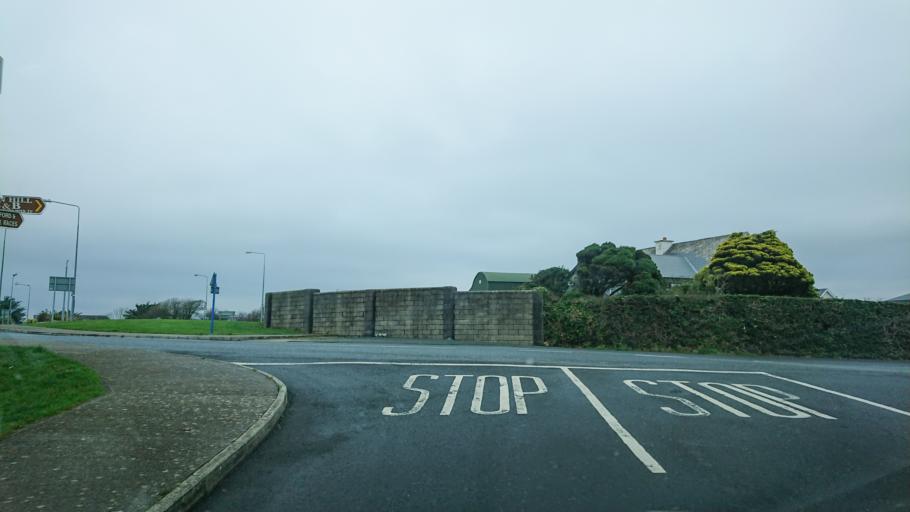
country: IE
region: Munster
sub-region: Waterford
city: Tra Mhor
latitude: 52.1538
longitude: -7.1685
